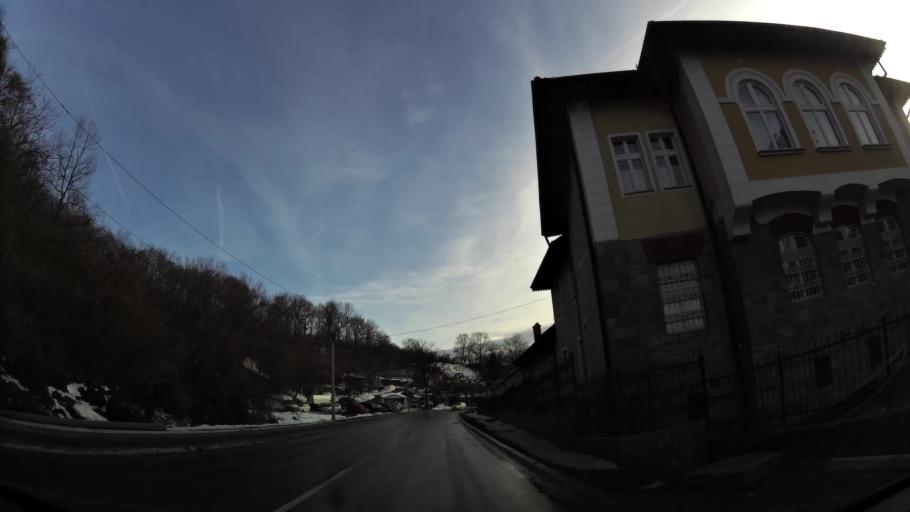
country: RS
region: Central Serbia
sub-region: Belgrade
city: Rakovica
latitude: 44.7310
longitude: 20.4474
